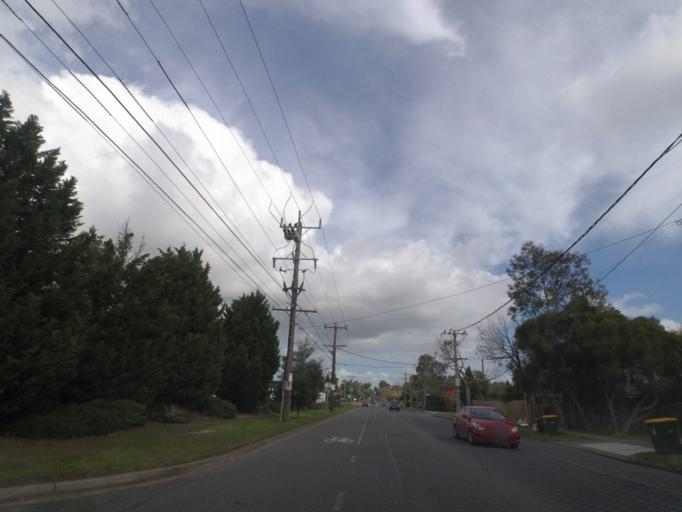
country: AU
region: Victoria
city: Mitcham
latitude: -37.8306
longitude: 145.2134
